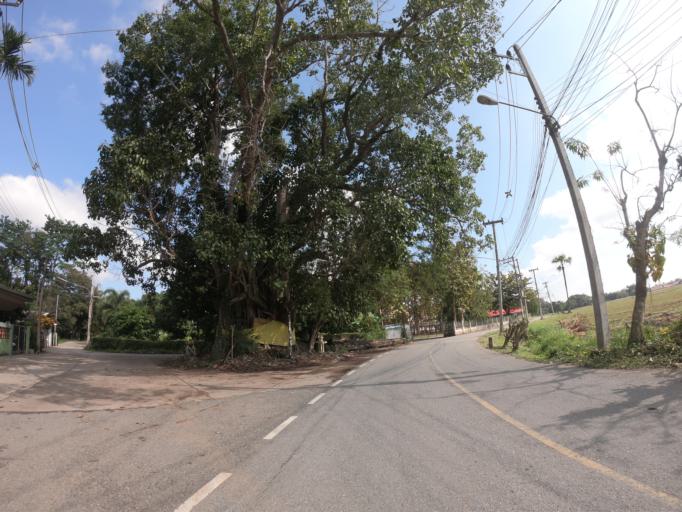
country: TH
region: Chiang Mai
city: San Sai
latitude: 18.8499
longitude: 99.0470
